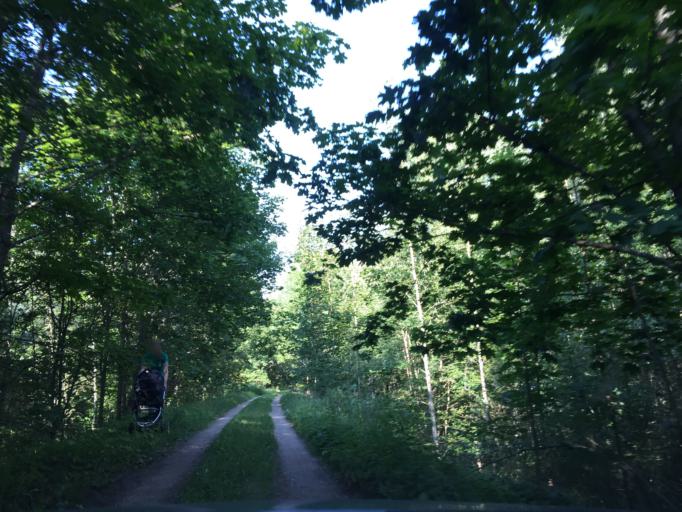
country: LV
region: Limbazu Rajons
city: Limbazi
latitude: 57.5635
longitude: 24.7874
